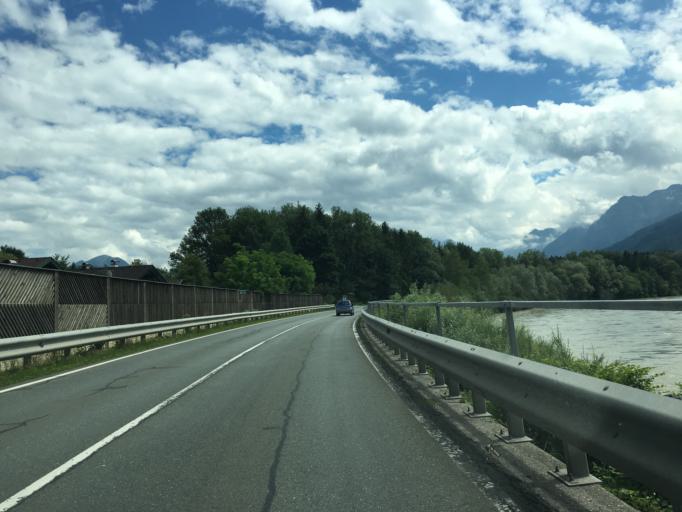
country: AT
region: Salzburg
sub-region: Politischer Bezirk Hallein
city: Adnet
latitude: 47.6701
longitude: 13.1212
